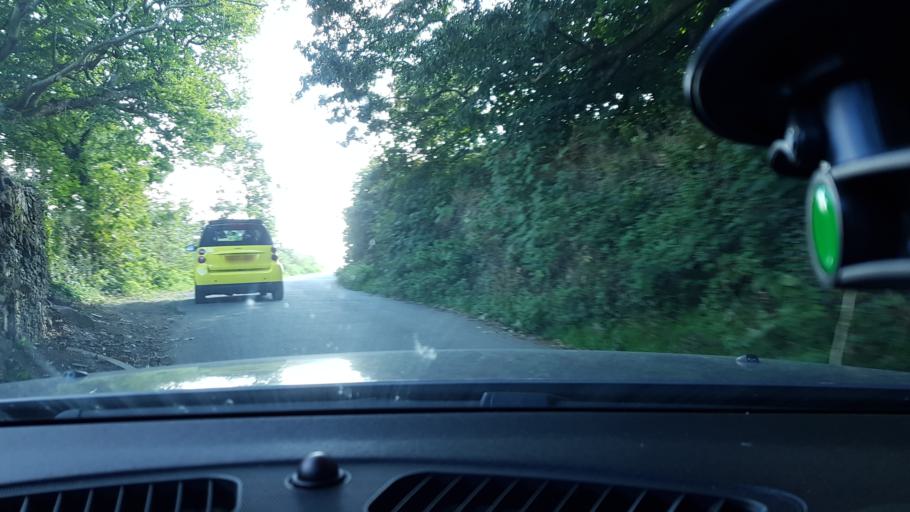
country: GB
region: England
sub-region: Cornwall
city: Tintagel
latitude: 50.6628
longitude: -4.7541
